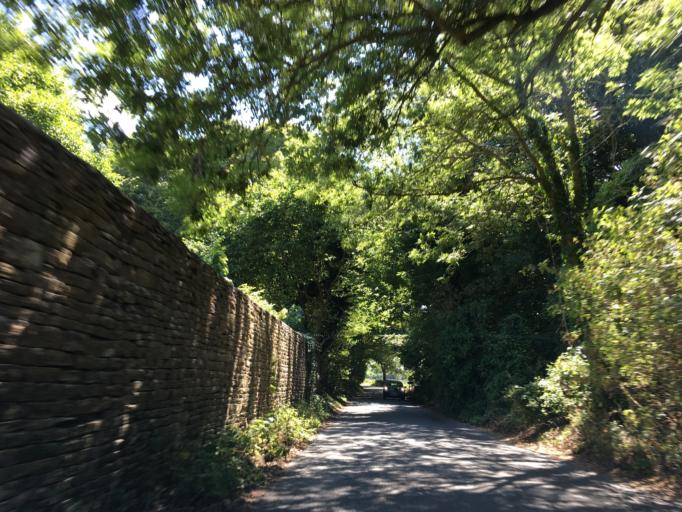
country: GB
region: England
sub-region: Gloucestershire
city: Chalford
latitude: 51.7505
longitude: -2.1394
